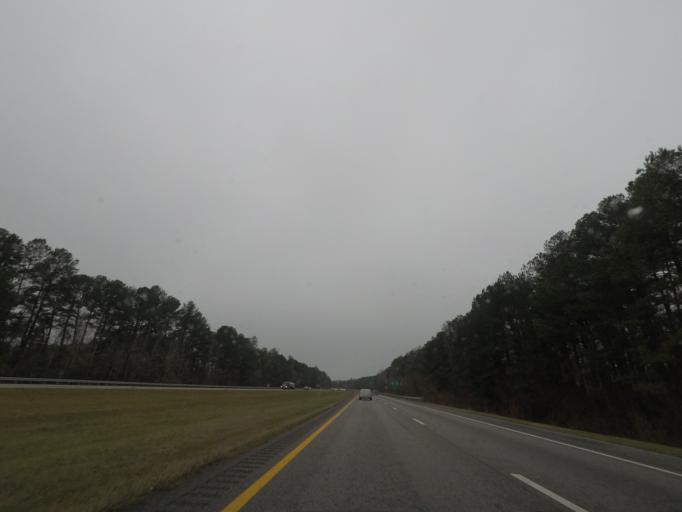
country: US
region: South Carolina
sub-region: Florence County
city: Timmonsville
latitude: 33.9829
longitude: -80.0303
